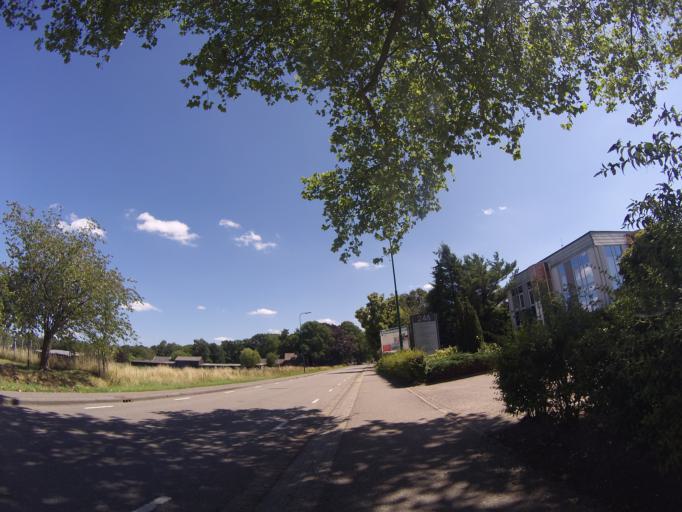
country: NL
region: Utrecht
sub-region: Gemeente De Bilt
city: De Bilt
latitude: 52.1181
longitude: 5.1696
